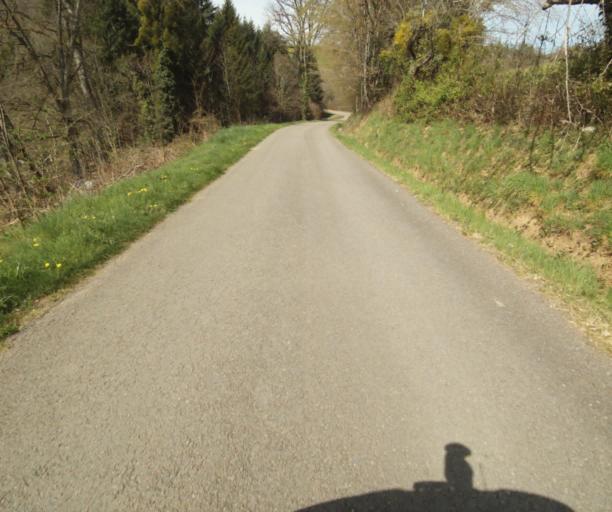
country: FR
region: Limousin
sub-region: Departement de la Correze
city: Naves
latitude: 45.3612
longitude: 1.7996
